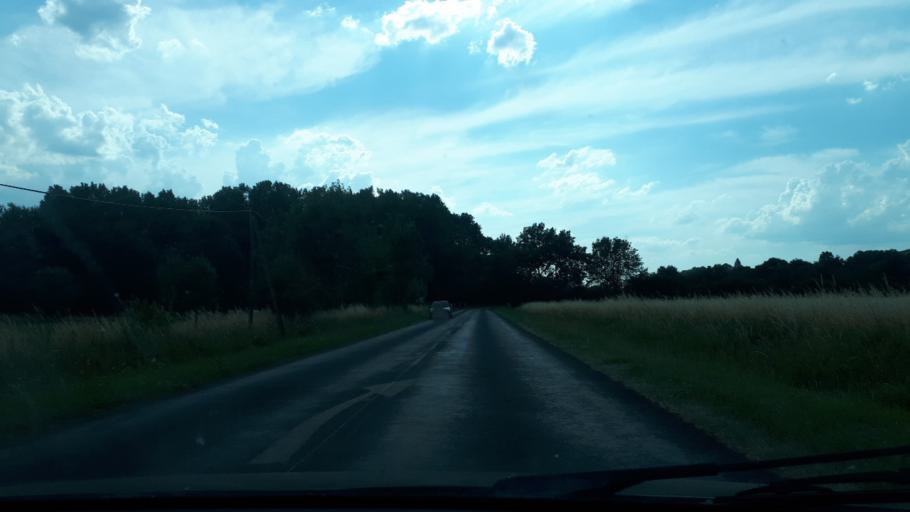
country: FR
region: Centre
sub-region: Departement du Loir-et-Cher
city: Montoire-sur-le-Loir
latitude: 47.7730
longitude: 0.8152
